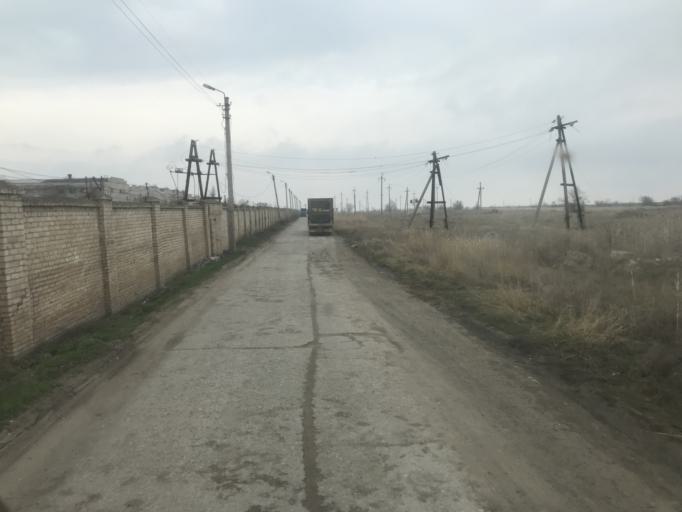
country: RU
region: Volgograd
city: Krasnoslobodsk
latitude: 48.5330
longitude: 44.5856
